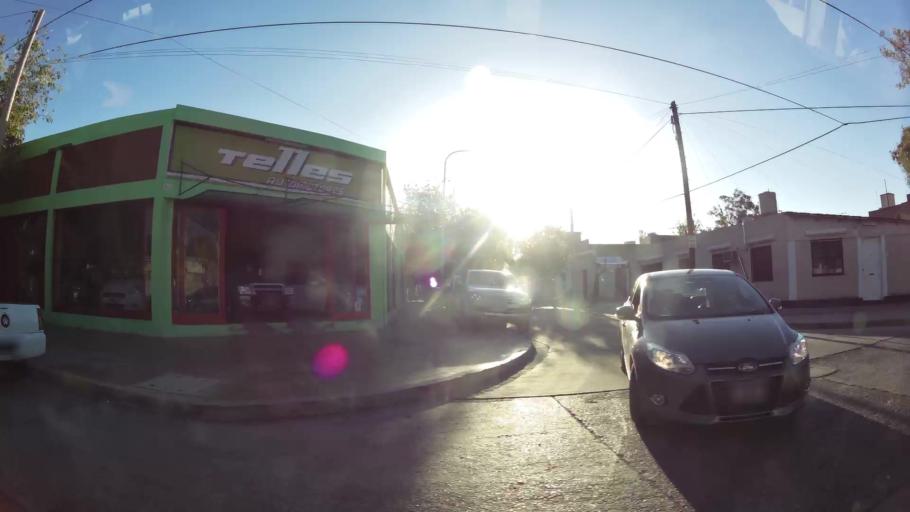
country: AR
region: San Juan
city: San Juan
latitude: -31.5504
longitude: -68.5245
